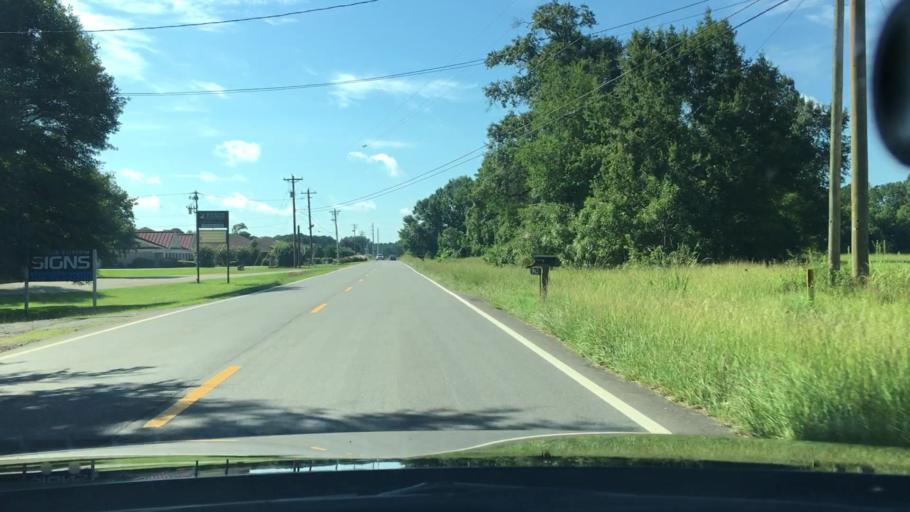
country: US
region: Georgia
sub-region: Putnam County
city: Jefferson
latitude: 33.4261
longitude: -83.2724
